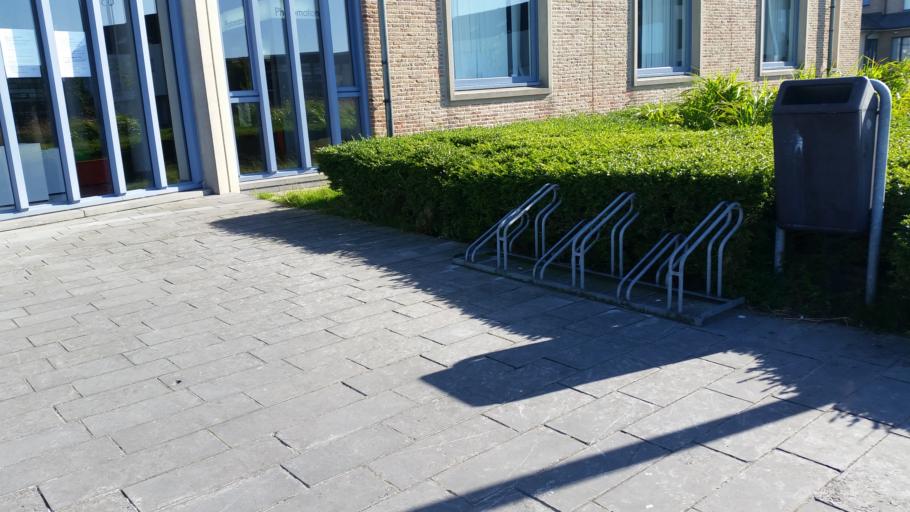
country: BE
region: Flanders
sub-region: Provincie West-Vlaanderen
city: Bredene
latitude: 51.2406
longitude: 2.9651
